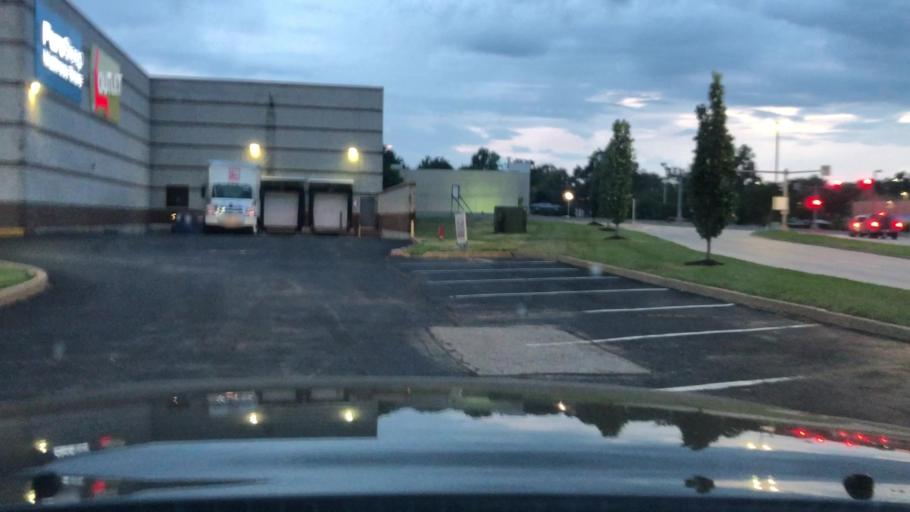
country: US
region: Missouri
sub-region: Saint Louis County
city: Saint Ann
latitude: 38.7341
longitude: -90.4022
